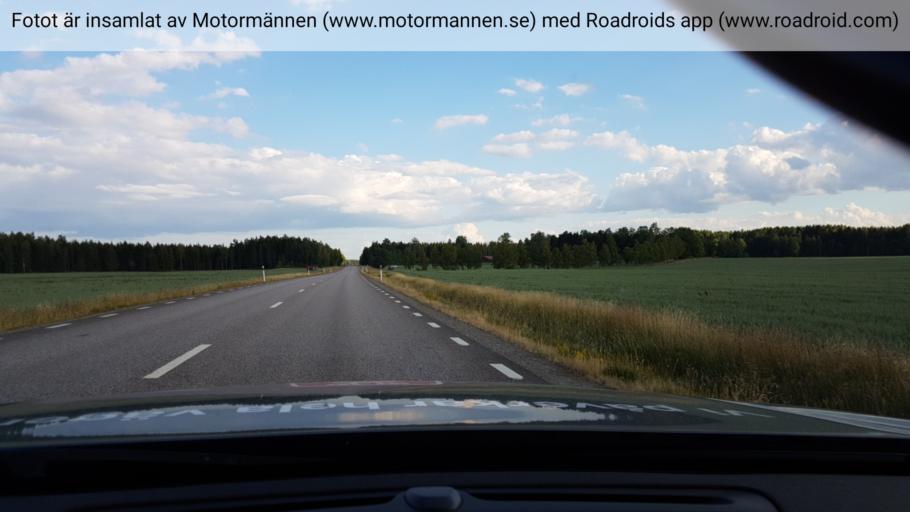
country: SE
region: Uppsala
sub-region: Heby Kommun
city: Morgongava
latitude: 59.8770
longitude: 16.9217
